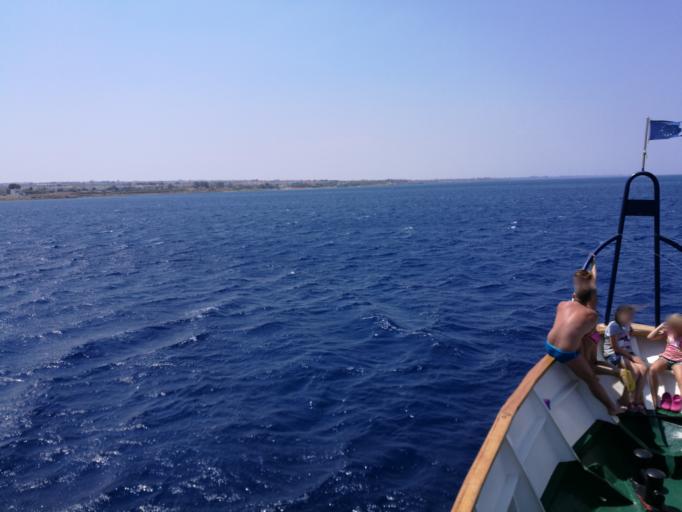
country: CY
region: Ammochostos
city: Protaras
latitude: 35.0482
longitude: 34.0378
